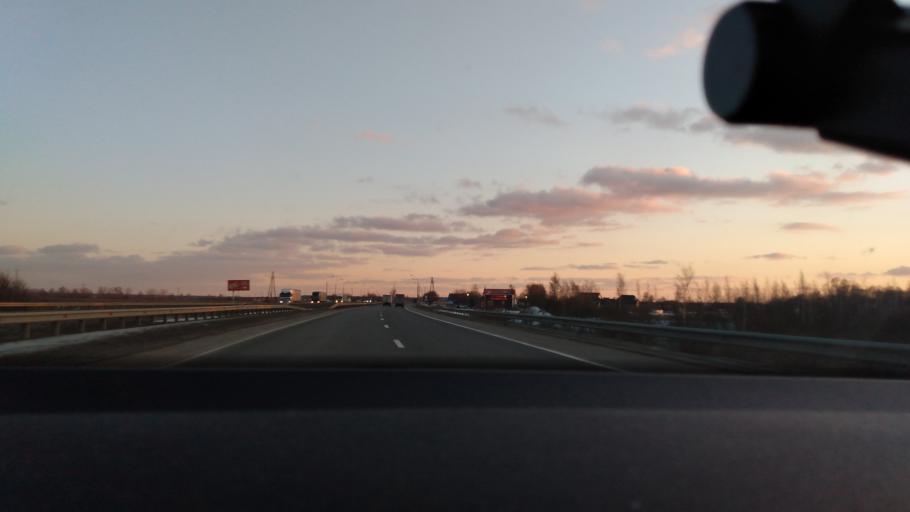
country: RU
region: Moskovskaya
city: Kolomna
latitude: 55.0967
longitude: 38.9027
